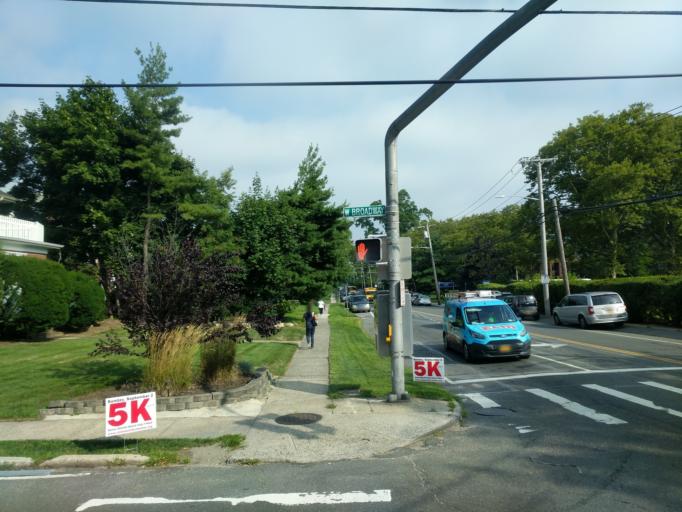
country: US
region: New York
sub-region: Nassau County
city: Woodmere
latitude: 40.6337
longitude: -73.7141
